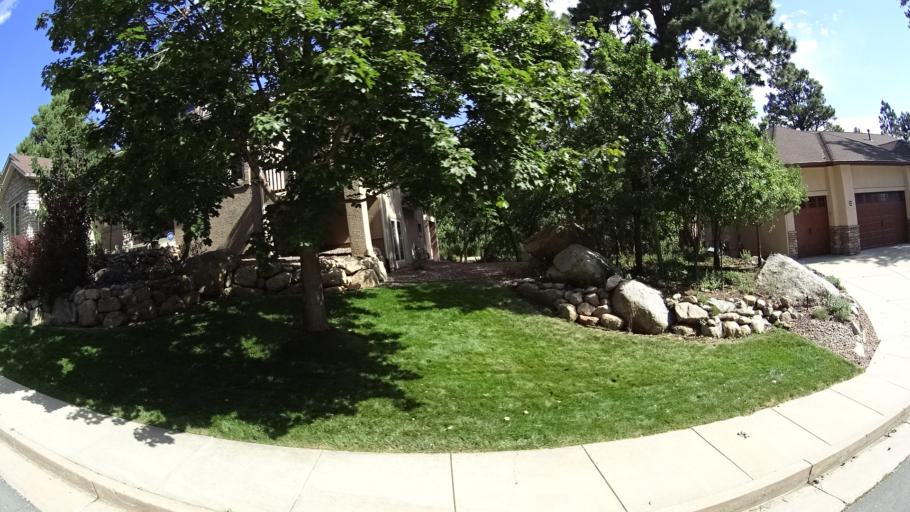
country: US
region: Colorado
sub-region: El Paso County
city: Fort Carson
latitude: 38.7540
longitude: -104.8401
